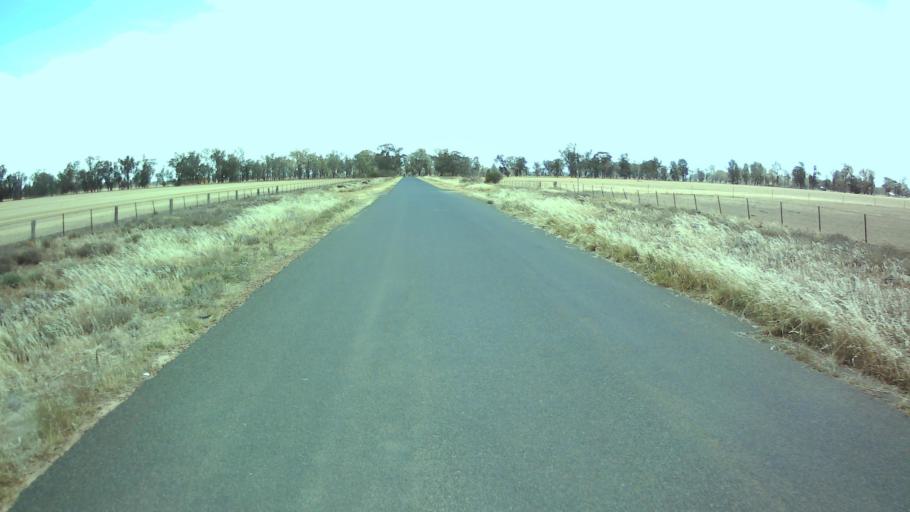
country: AU
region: New South Wales
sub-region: Weddin
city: Grenfell
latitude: -34.0715
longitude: 147.7774
